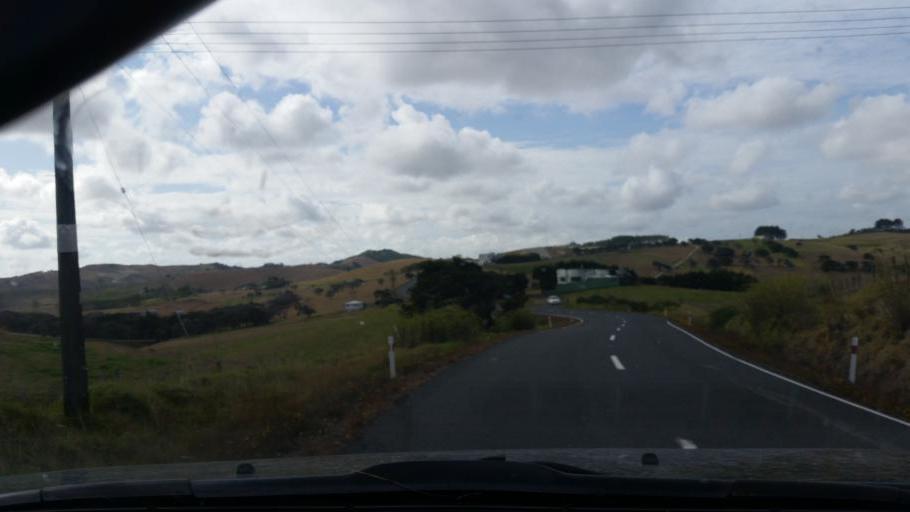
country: NZ
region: Northland
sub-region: Kaipara District
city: Dargaville
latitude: -35.9640
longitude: 173.9296
